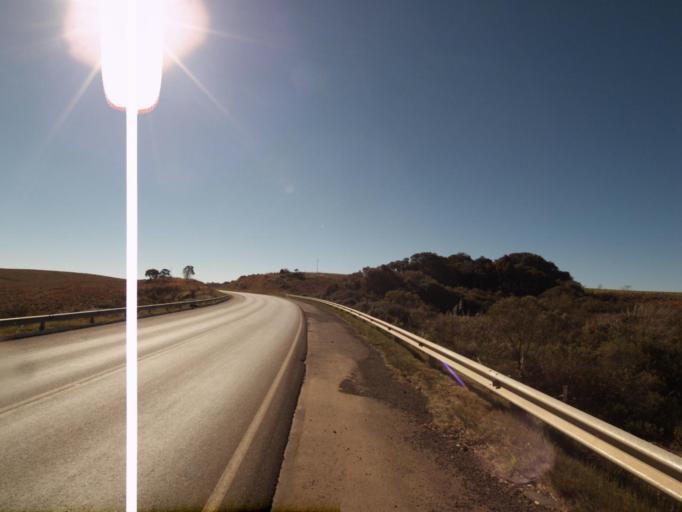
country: BR
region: Santa Catarina
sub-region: Joacaba
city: Joacaba
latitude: -26.7957
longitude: -51.6942
